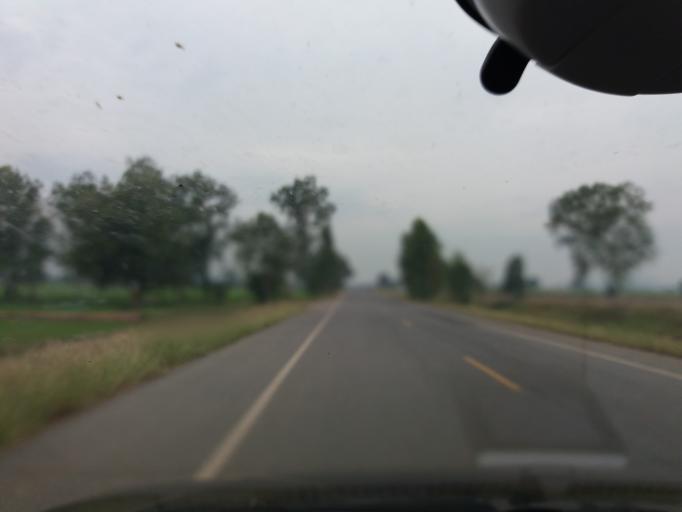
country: TH
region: Suphan Buri
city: Doem Bang Nang Buat
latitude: 14.8656
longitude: 100.1307
